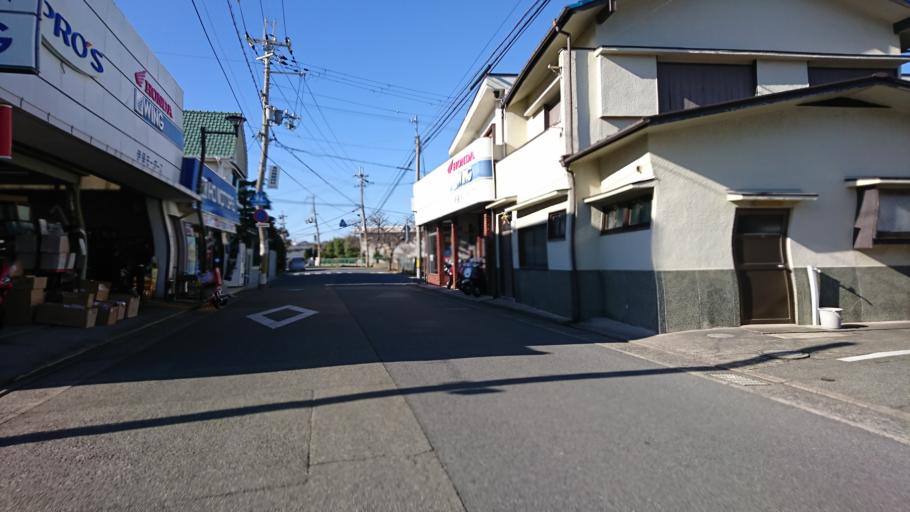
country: JP
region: Hyogo
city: Kakogawacho-honmachi
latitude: 34.7672
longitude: 134.7855
